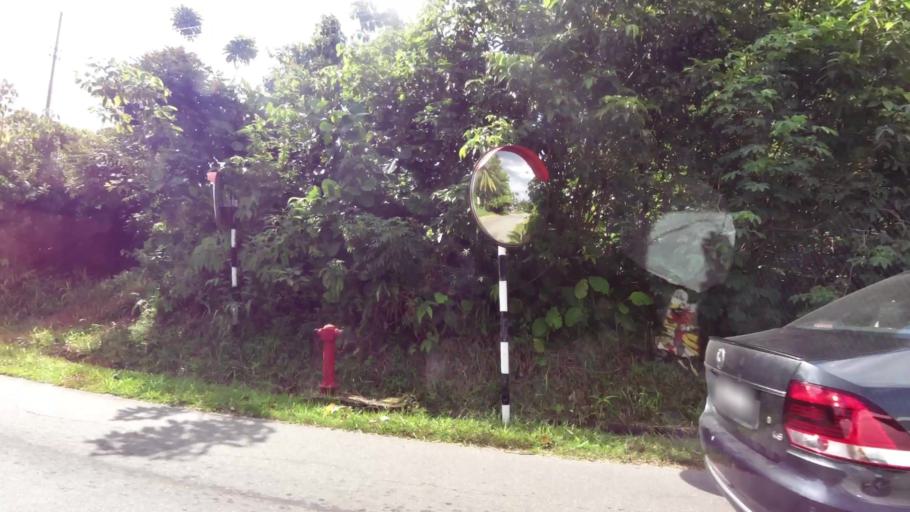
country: BN
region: Brunei and Muara
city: Bandar Seri Begawan
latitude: 4.9561
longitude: 114.9524
